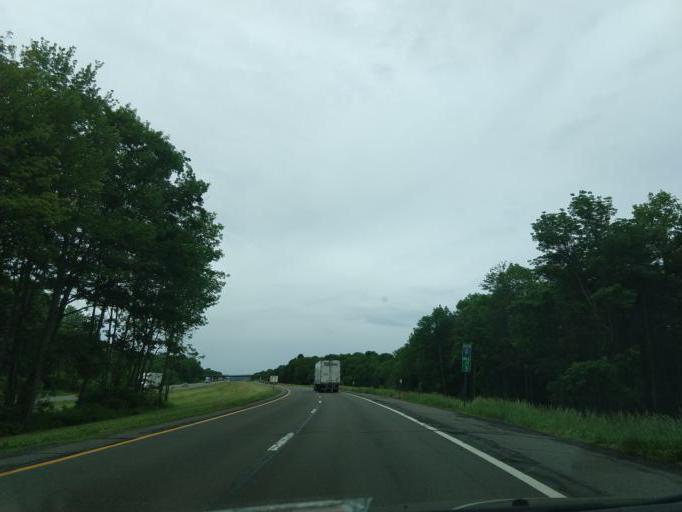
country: US
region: New York
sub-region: Chenango County
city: Lakeview
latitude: 42.3234
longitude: -75.9772
